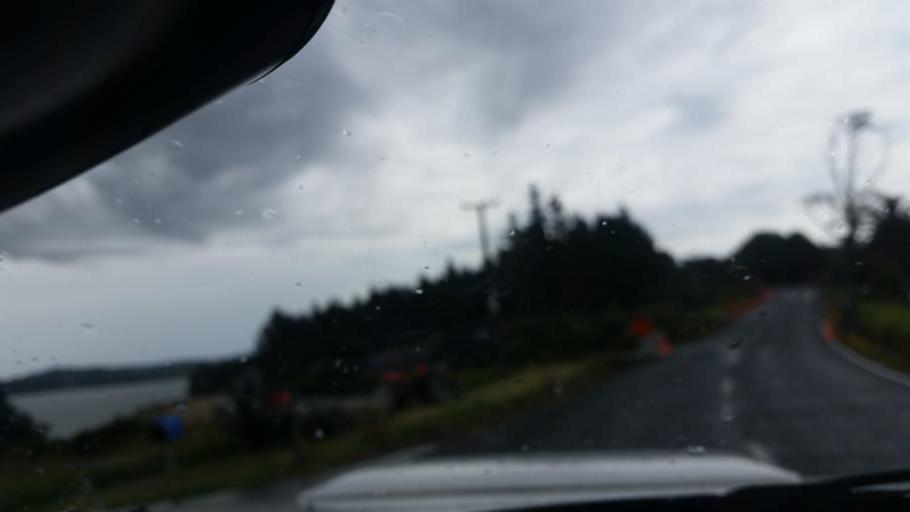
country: NZ
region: Auckland
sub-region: Auckland
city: Wellsford
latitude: -36.1521
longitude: 174.2216
